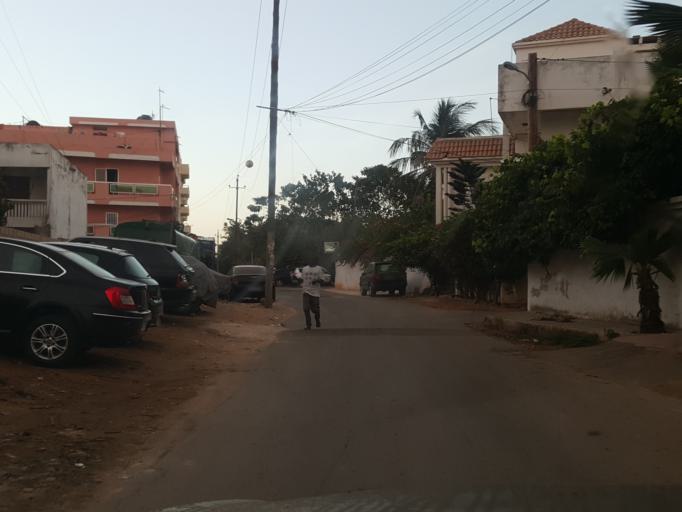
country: SN
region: Dakar
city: Grand Dakar
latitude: 14.7342
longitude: -17.4620
